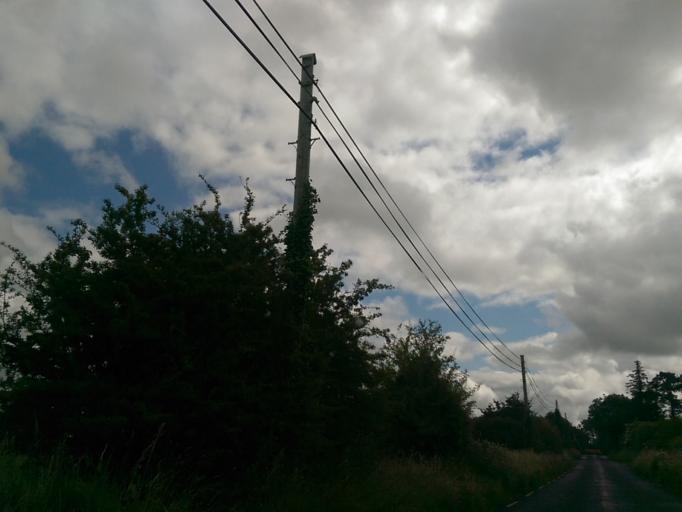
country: IE
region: Connaught
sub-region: County Galway
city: Loughrea
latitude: 53.4249
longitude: -8.5035
